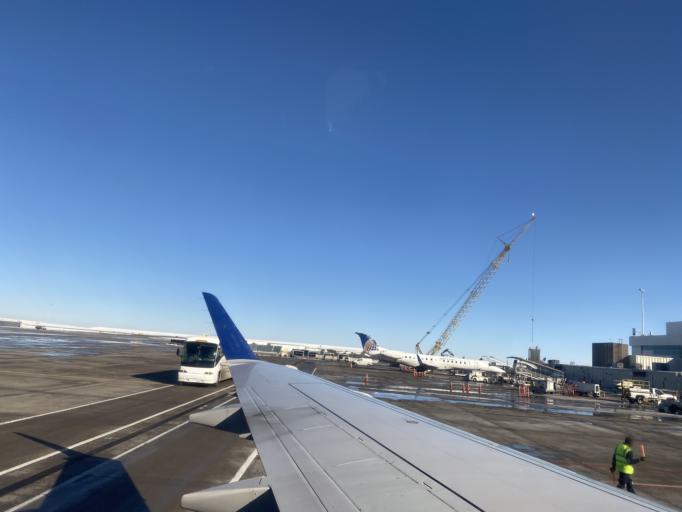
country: US
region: Colorado
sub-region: Weld County
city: Lochbuie
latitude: 39.8596
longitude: -104.6696
